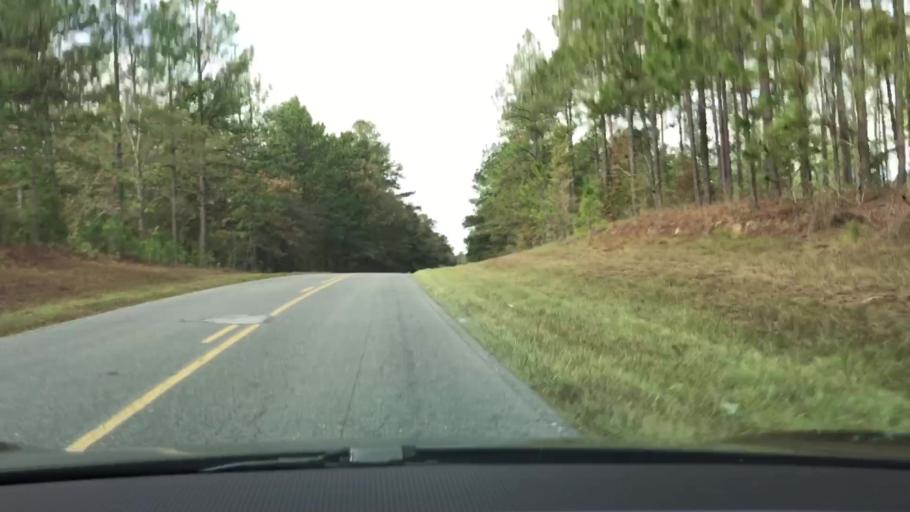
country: US
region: Georgia
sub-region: Jefferson County
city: Wadley
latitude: 32.7992
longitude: -82.3597
